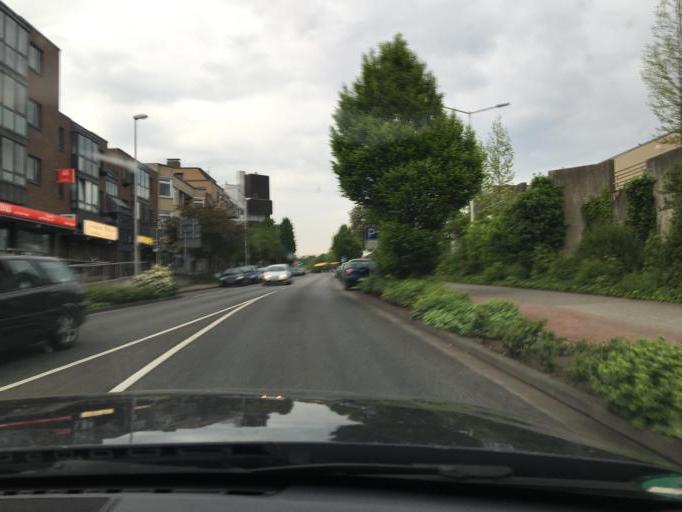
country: DE
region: North Rhine-Westphalia
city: Emsdetten
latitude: 52.1747
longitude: 7.5322
